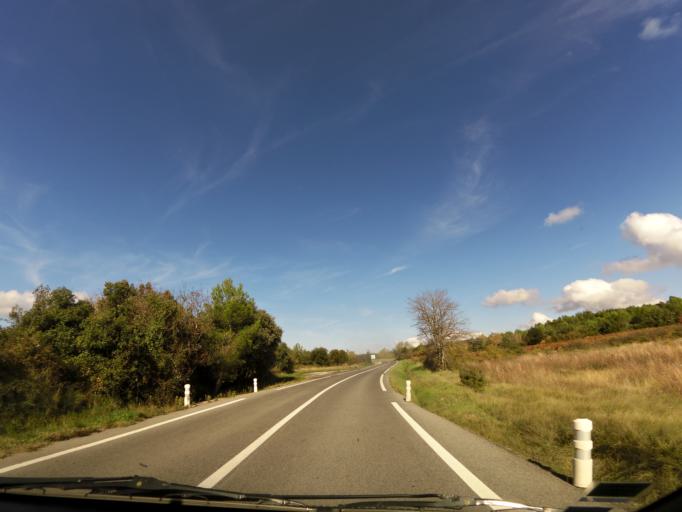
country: FR
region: Languedoc-Roussillon
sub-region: Departement du Gard
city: Villevieille
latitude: 43.8635
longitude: 4.0990
